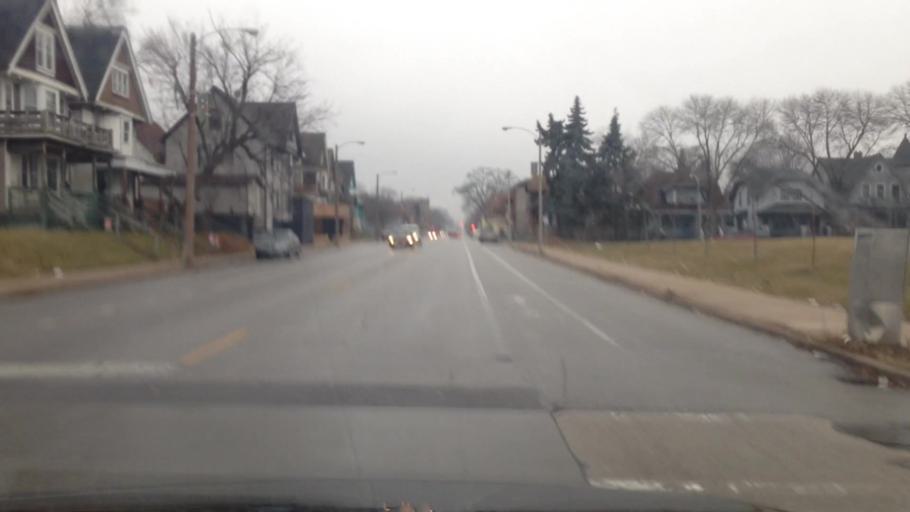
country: US
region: Wisconsin
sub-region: Milwaukee County
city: Wauwatosa
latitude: 43.0679
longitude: -87.9575
